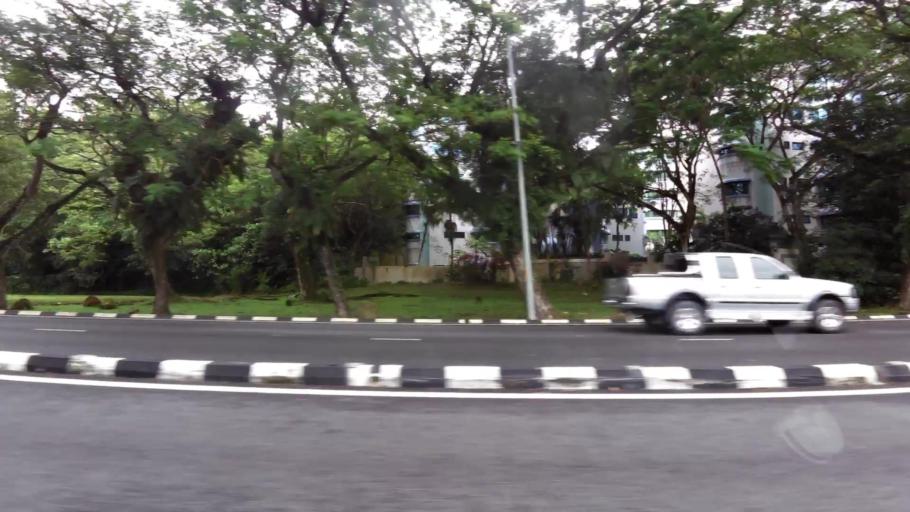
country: BN
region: Brunei and Muara
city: Bandar Seri Begawan
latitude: 4.9021
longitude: 114.9340
